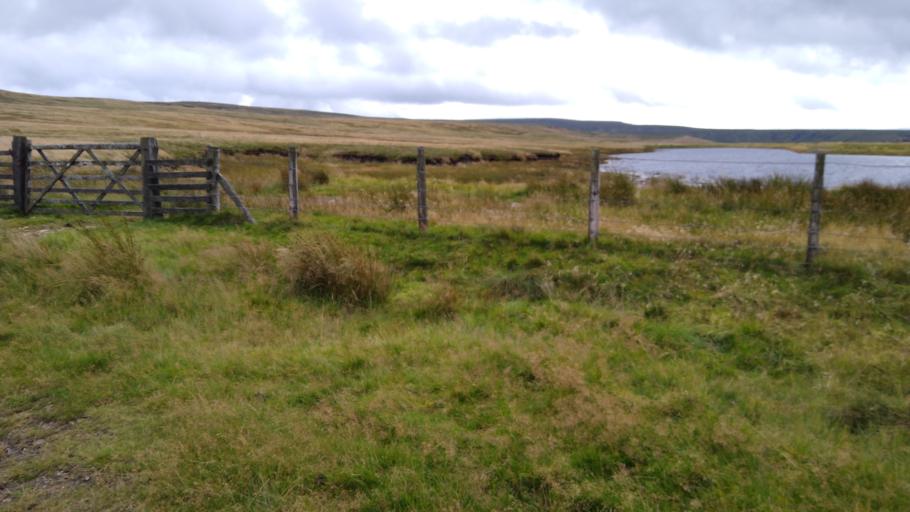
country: GB
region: England
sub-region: Northumberland
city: Bardon Mill
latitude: 54.7700
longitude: -2.3338
